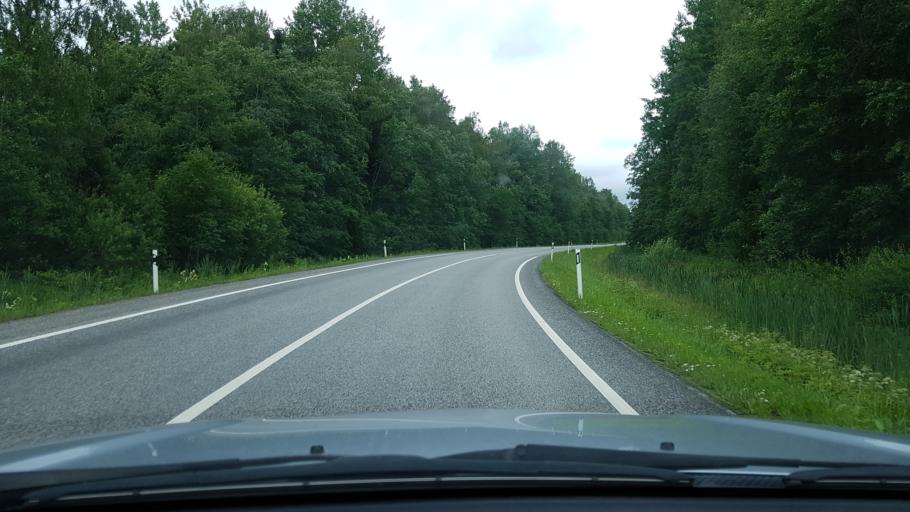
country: EE
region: Ida-Virumaa
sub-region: Narva-Joesuu linn
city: Narva-Joesuu
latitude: 59.3625
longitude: 27.9327
